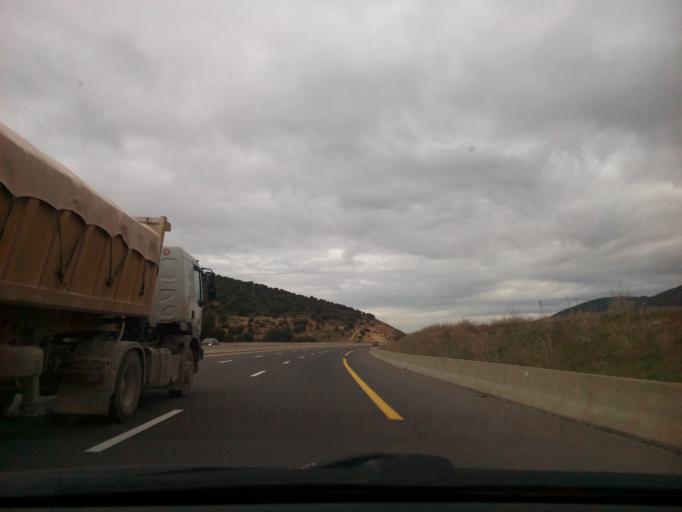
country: DZ
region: Sidi Bel Abbes
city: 'Ain el Berd
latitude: 35.4087
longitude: -0.4899
